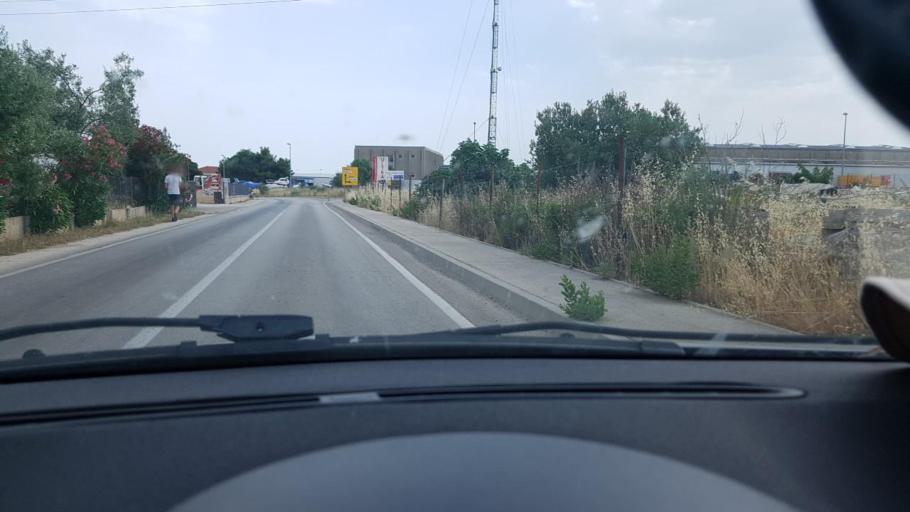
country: HR
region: Sibensko-Kniniska
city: Vodice
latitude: 43.7707
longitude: 15.7729
